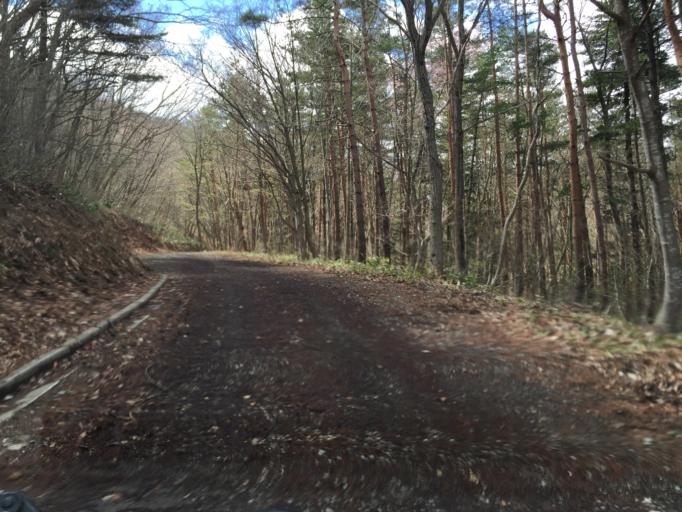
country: JP
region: Fukushima
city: Fukushima-shi
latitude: 37.8592
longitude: 140.4204
